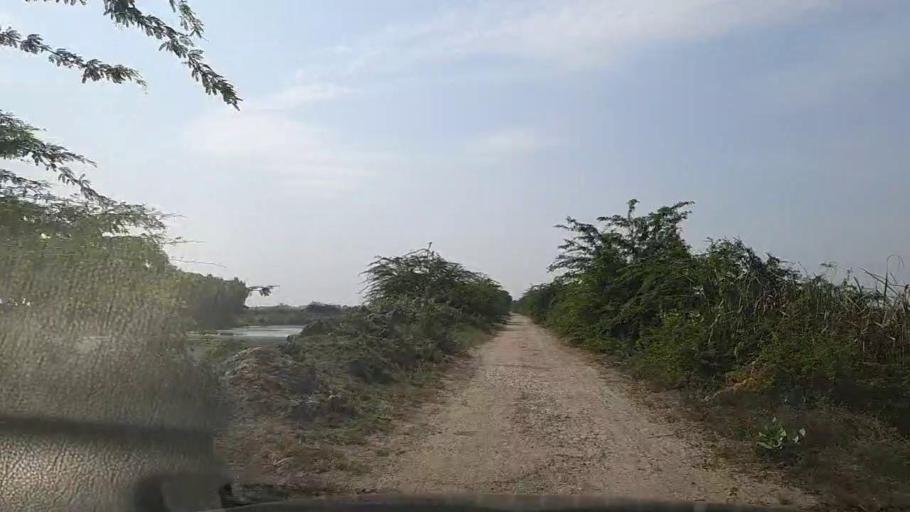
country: PK
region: Sindh
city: Thatta
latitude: 24.7653
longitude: 67.7928
